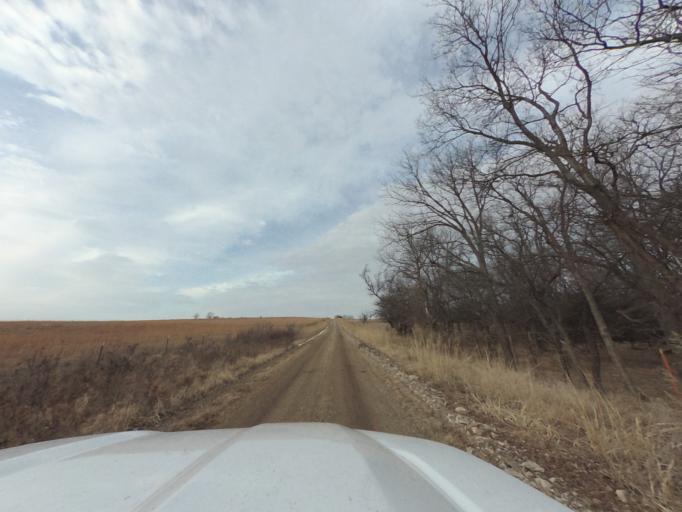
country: US
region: Kansas
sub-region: Chase County
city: Cottonwood Falls
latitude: 38.4783
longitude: -96.4427
